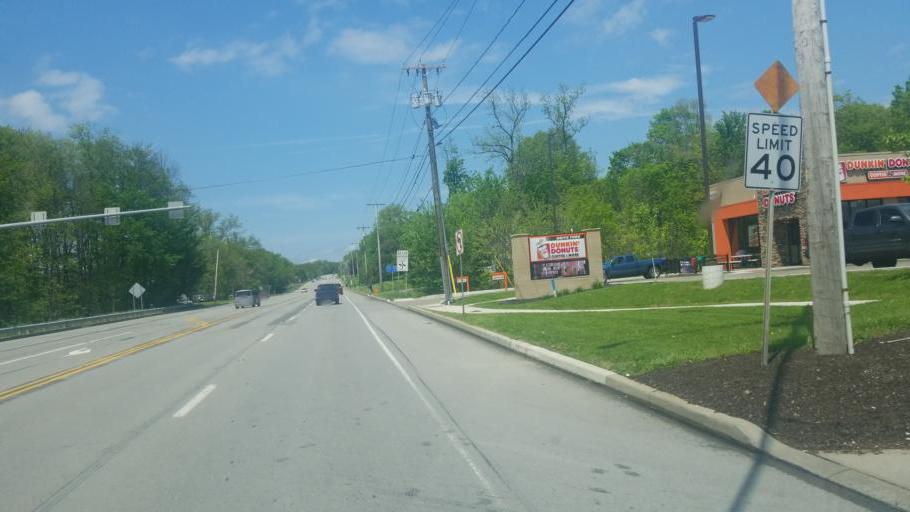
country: US
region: Pennsylvania
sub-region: Mercer County
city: Hermitage
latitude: 41.2020
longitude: -80.4565
